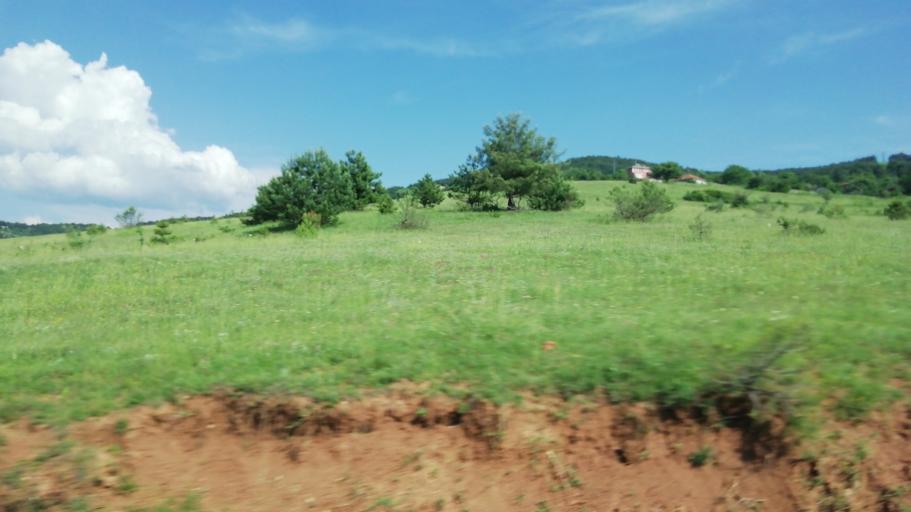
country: TR
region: Karabuk
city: Karabuk
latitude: 41.1284
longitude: 32.5758
